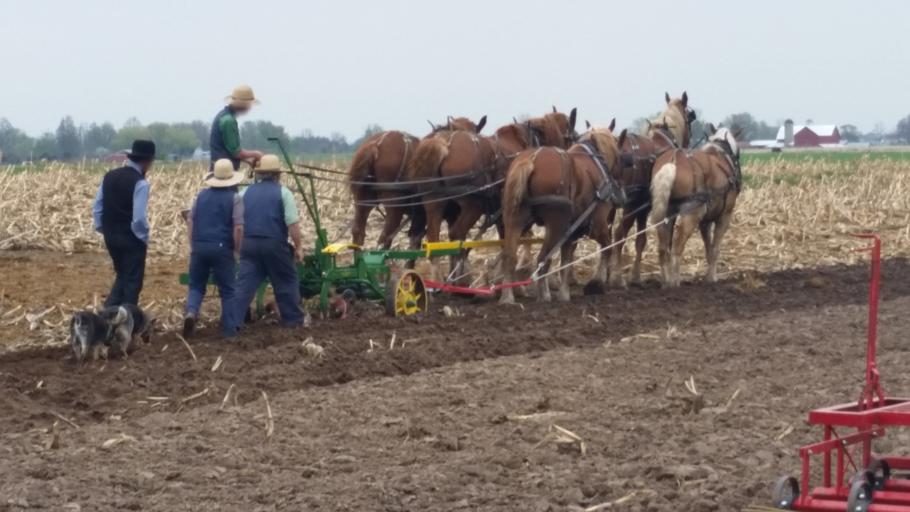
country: US
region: Michigan
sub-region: Gladwin County
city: Gladwin
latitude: 44.0470
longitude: -84.4822
